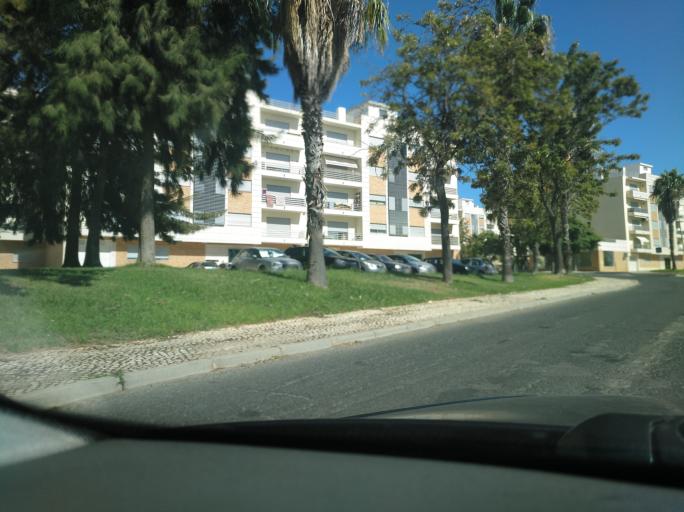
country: PT
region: Faro
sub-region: Olhao
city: Olhao
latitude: 37.0412
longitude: -7.8523
